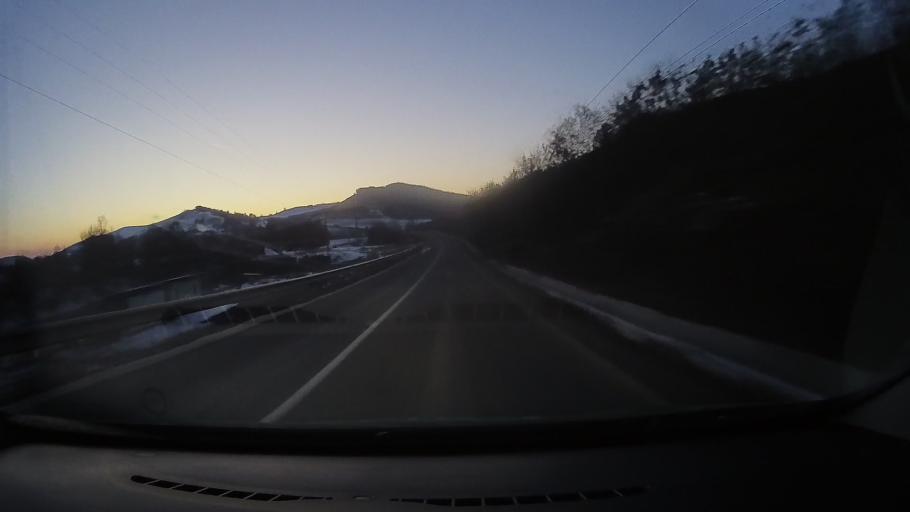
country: RO
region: Sibiu
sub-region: Comuna Alma
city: Alma
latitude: 46.2030
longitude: 24.4614
